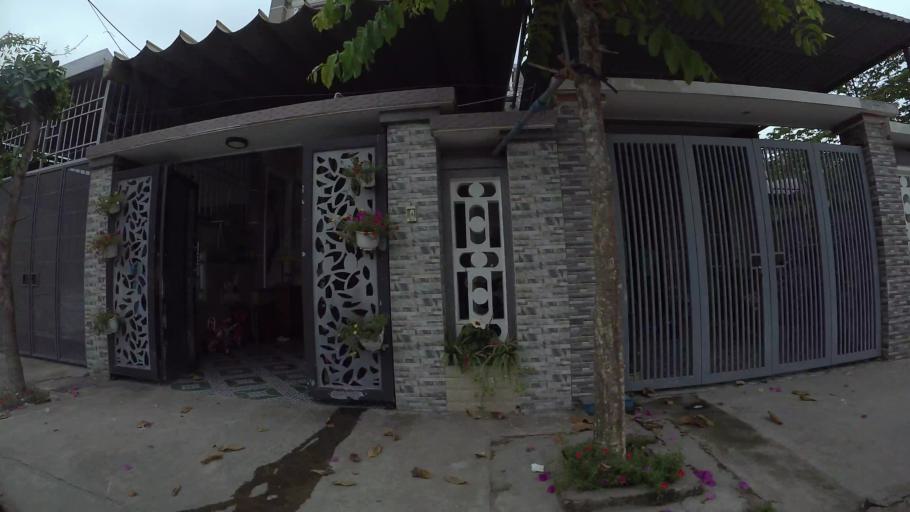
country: VN
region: Da Nang
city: Thanh Khe
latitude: 16.0441
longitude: 108.1739
